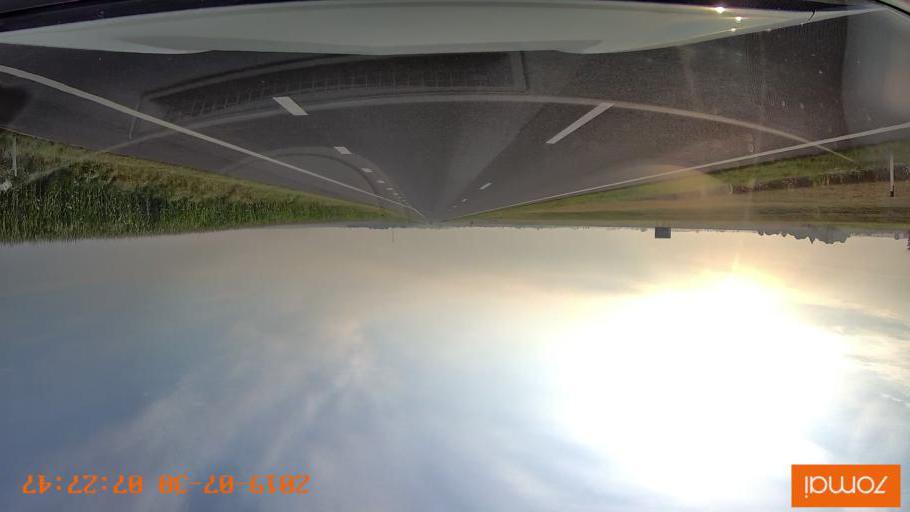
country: RU
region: Kaliningrad
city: Gvardeysk
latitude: 54.6805
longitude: 20.8962
